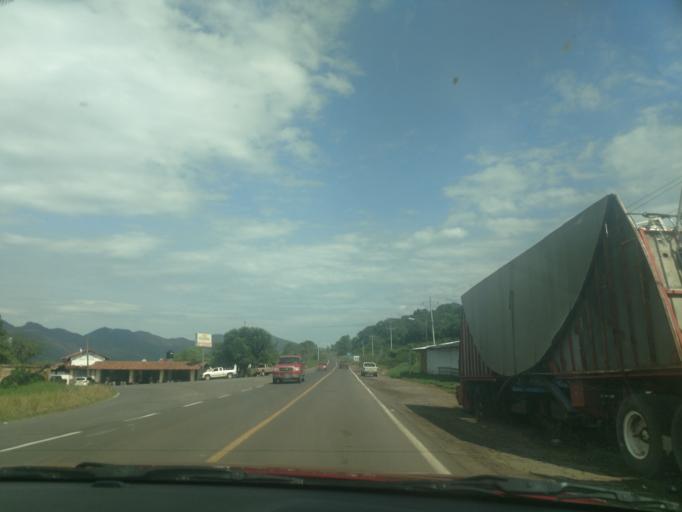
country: MX
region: Jalisco
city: Mascota
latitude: 20.4437
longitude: -104.7536
